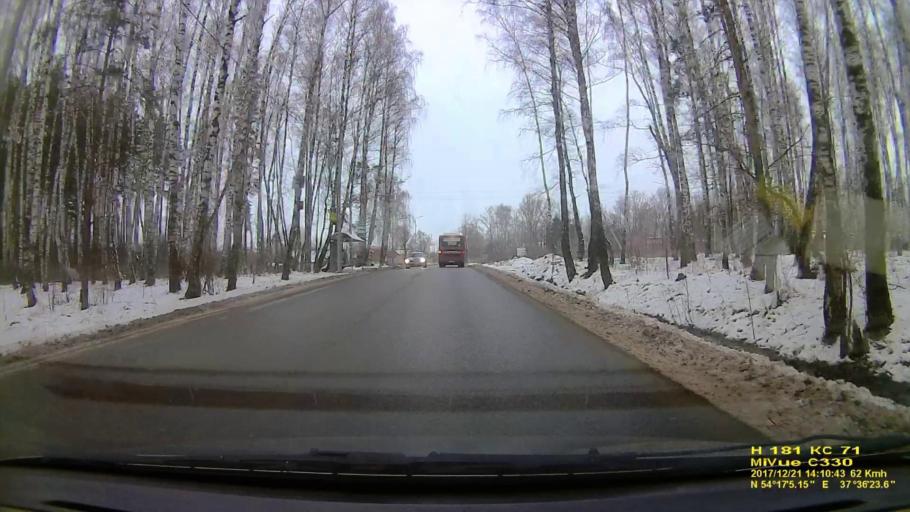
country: RU
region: Tula
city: Gorelki
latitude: 54.2850
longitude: 37.6066
